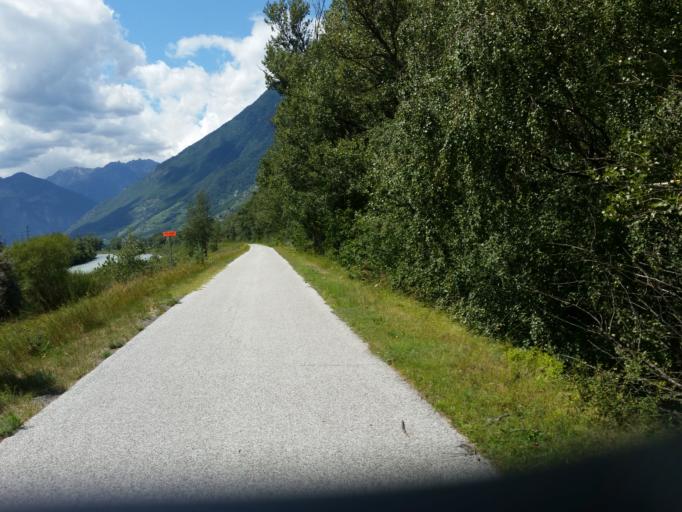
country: CH
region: Valais
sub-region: Martigny District
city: Saxon
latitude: 46.1584
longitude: 7.1766
